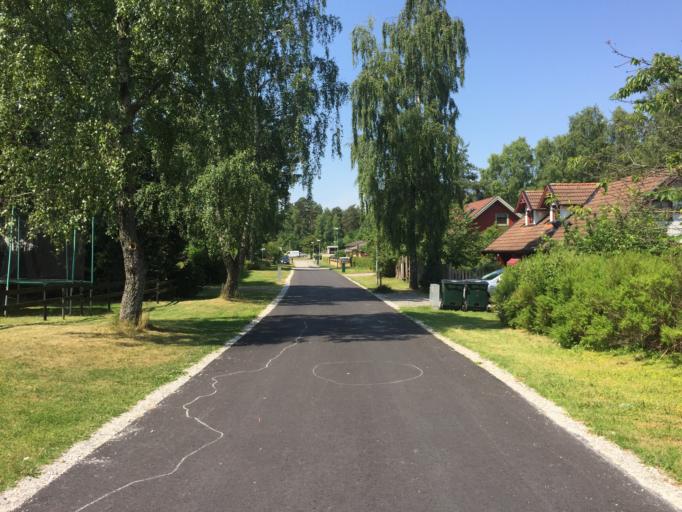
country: SE
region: Skane
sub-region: Lunds Kommun
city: Veberod
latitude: 55.6220
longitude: 13.5127
